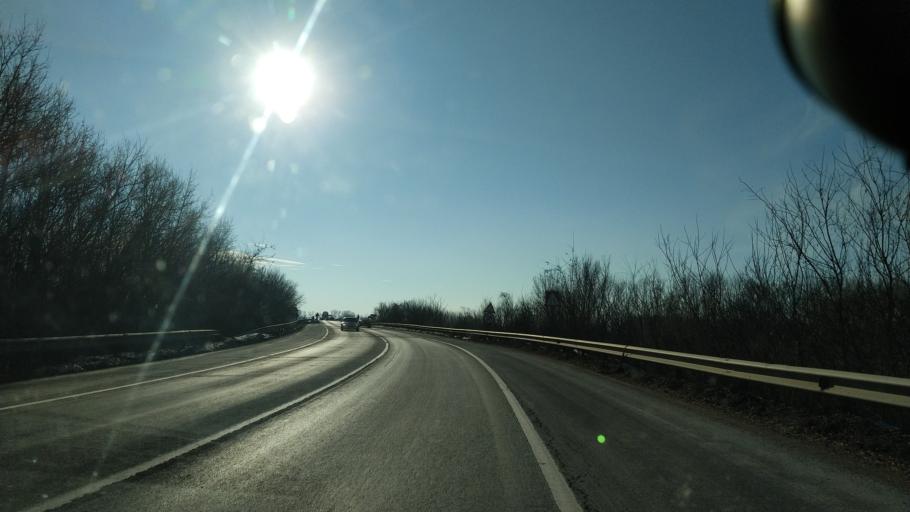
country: RO
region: Iasi
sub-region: Comuna Butea
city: Butea
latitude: 47.0866
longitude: 26.9024
